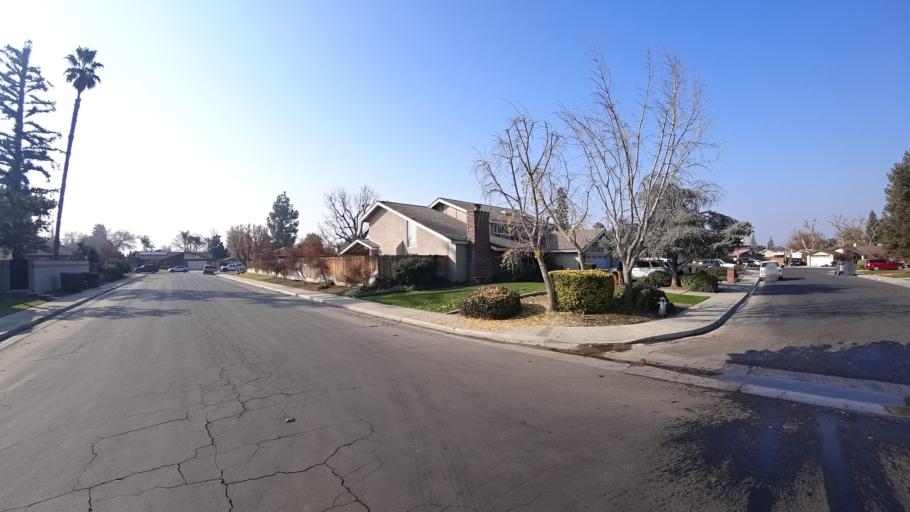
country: US
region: California
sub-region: Kern County
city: Greenacres
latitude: 35.3352
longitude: -119.0875
